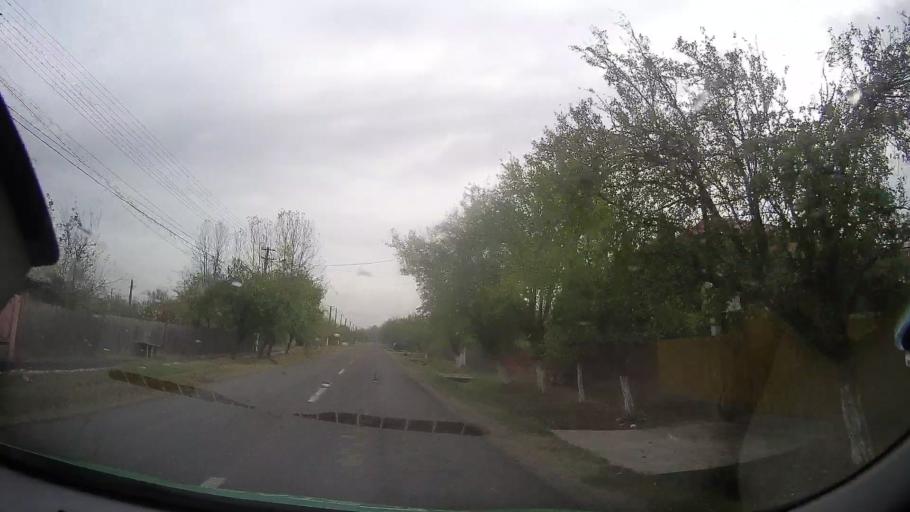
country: RO
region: Prahova
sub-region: Comuna Dumbrava
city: Dumbrava
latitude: 44.8655
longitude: 26.2017
